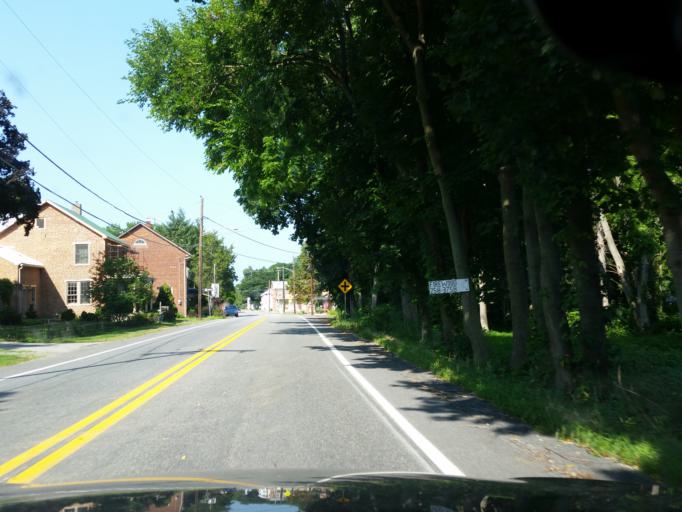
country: US
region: Pennsylvania
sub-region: Cumberland County
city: Boiling Springs
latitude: 40.1659
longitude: -77.0821
